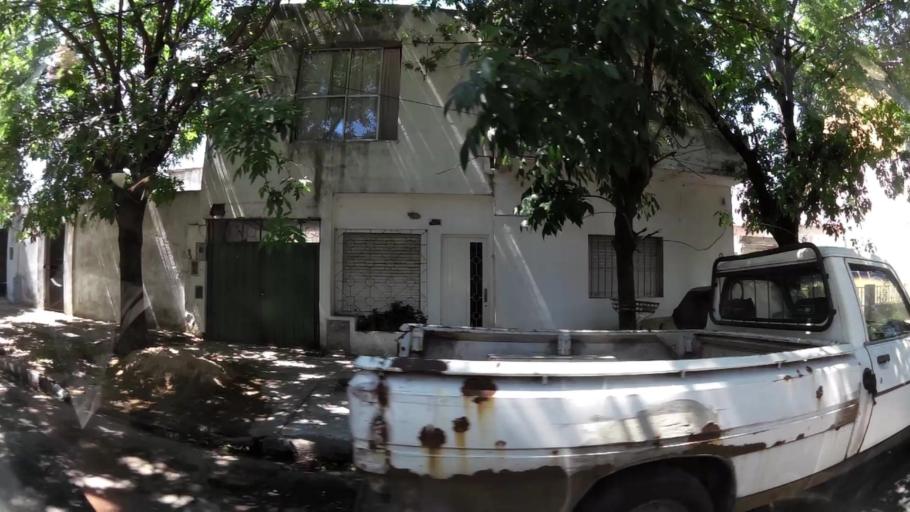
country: AR
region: Buenos Aires
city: Caseros
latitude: -34.5707
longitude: -58.5709
